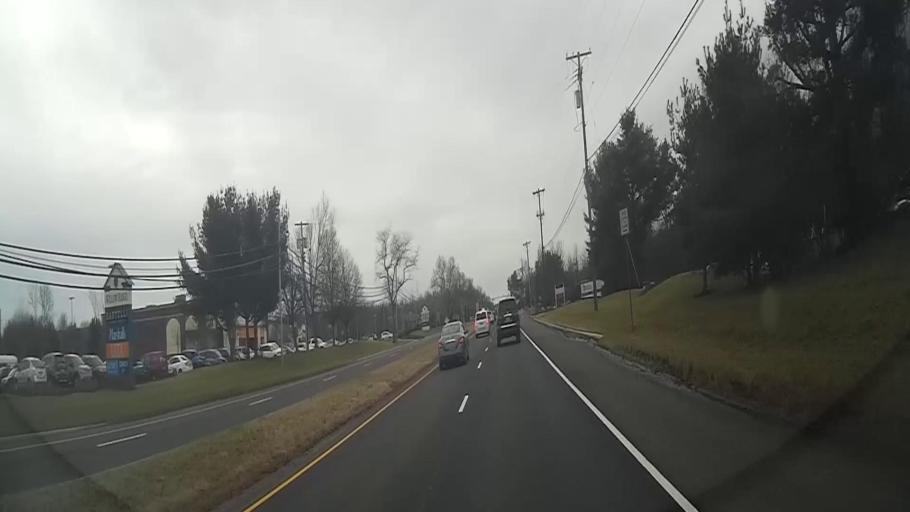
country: US
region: New Jersey
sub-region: Burlington County
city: Marlton
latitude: 39.8708
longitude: -74.9220
